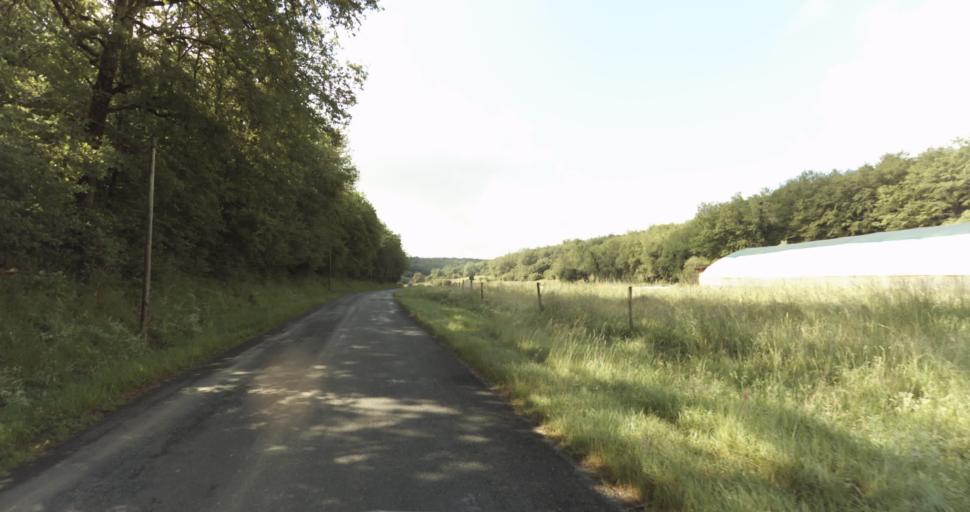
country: FR
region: Aquitaine
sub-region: Departement de la Dordogne
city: Lalinde
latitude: 44.8839
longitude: 0.7754
